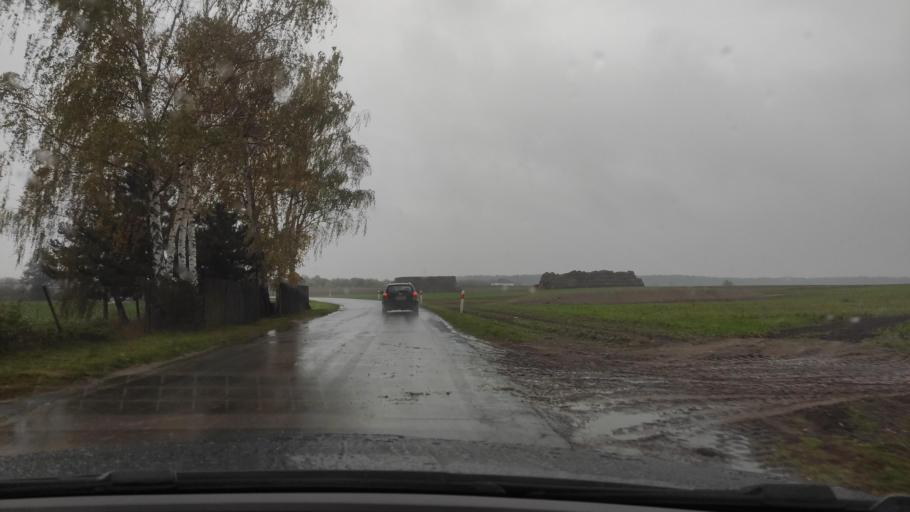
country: PL
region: Greater Poland Voivodeship
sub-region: Powiat poznanski
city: Kornik
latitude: 52.2140
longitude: 17.0987
